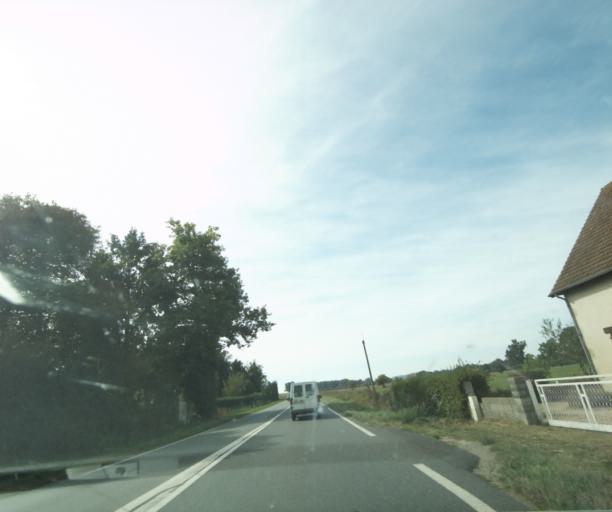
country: FR
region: Auvergne
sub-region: Departement de l'Allier
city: Saint-Gerand-le-Puy
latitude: 46.2053
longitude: 3.4999
